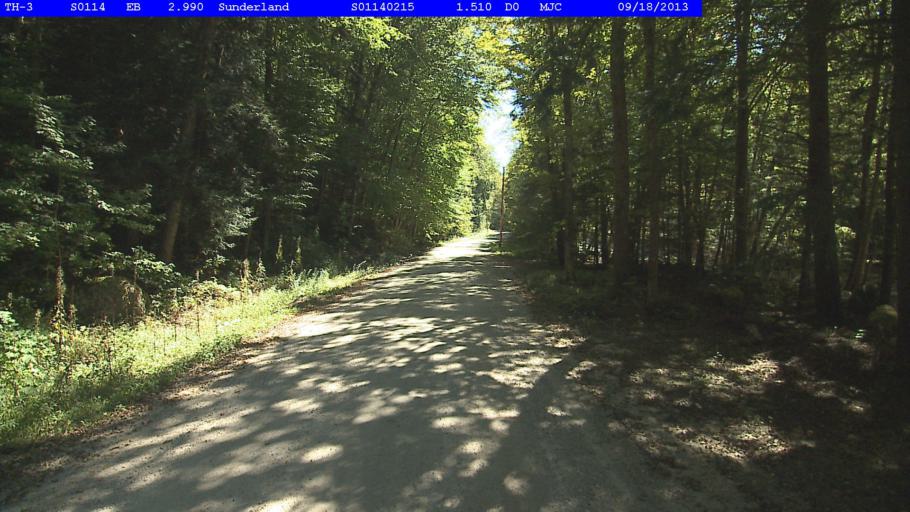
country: US
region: Vermont
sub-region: Bennington County
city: Arlington
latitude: 43.0517
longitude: -73.1153
